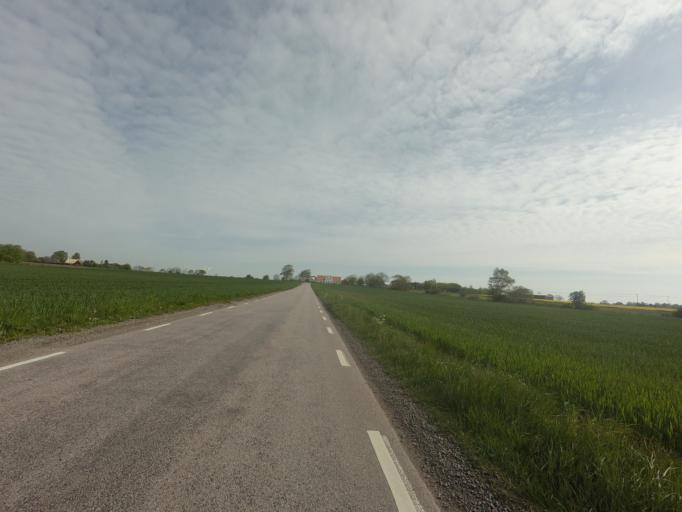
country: SE
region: Skane
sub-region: Hoganas Kommun
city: Hoganas
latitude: 56.2085
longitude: 12.5790
